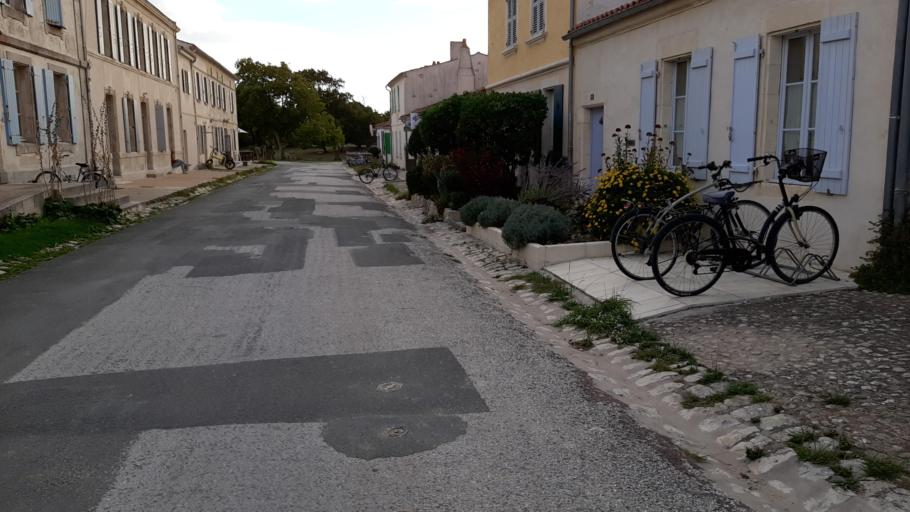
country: FR
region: Poitou-Charentes
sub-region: Departement de la Charente-Maritime
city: Boyard-Ville
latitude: 46.0117
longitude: -1.1741
